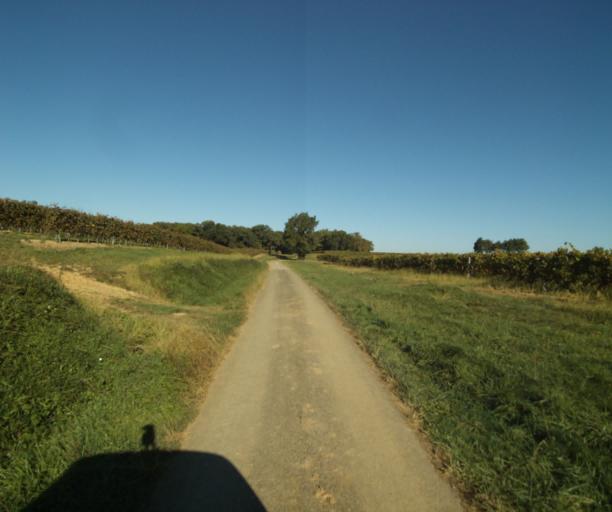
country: FR
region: Midi-Pyrenees
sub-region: Departement du Gers
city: Gondrin
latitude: 43.8373
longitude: 0.2703
